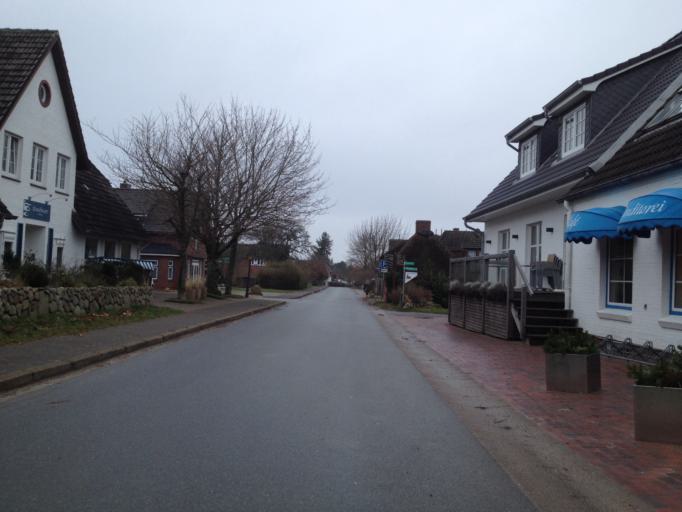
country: DE
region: Schleswig-Holstein
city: Nebel
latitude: 54.6518
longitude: 8.3536
